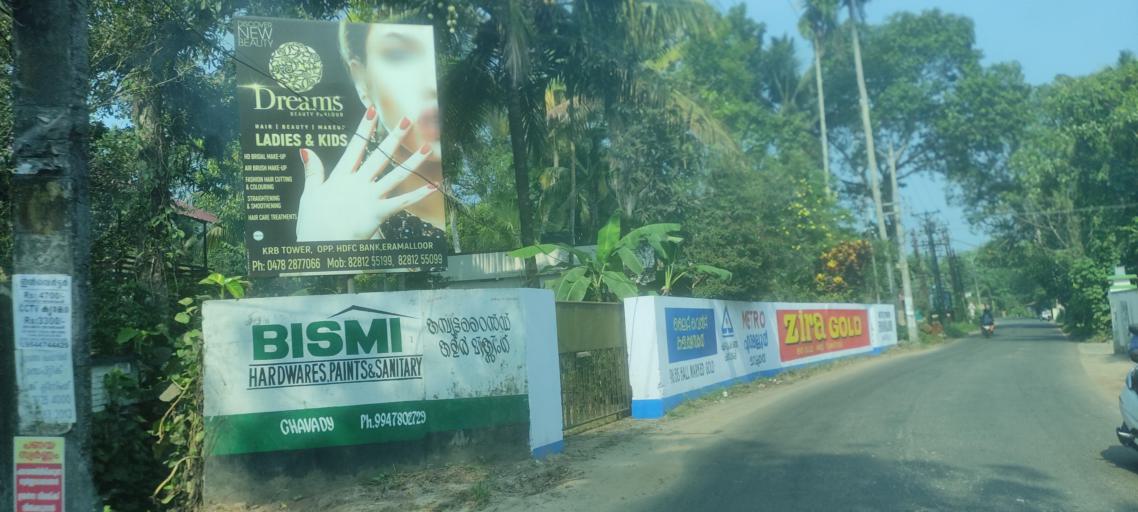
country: IN
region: Kerala
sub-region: Alappuzha
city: Kutiatodu
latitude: 9.7685
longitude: 76.3140
